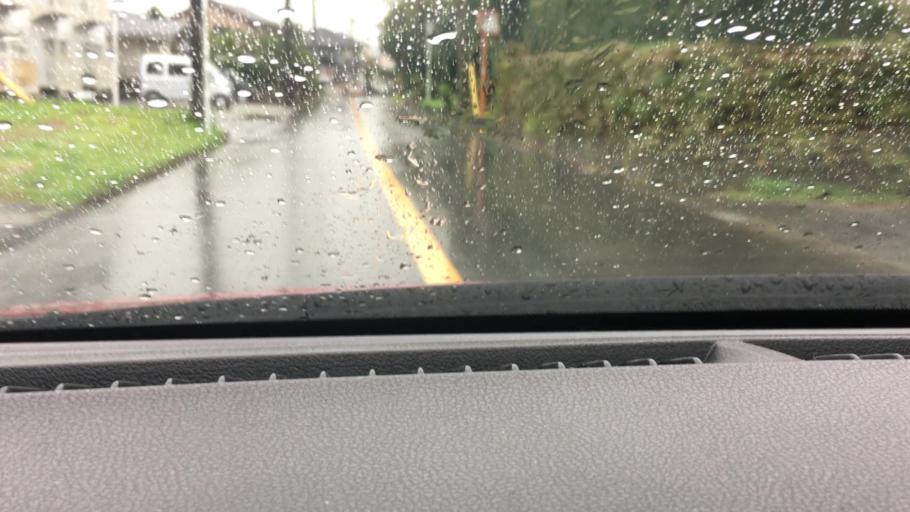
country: JP
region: Chiba
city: Kisarazu
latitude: 35.3734
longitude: 139.9506
